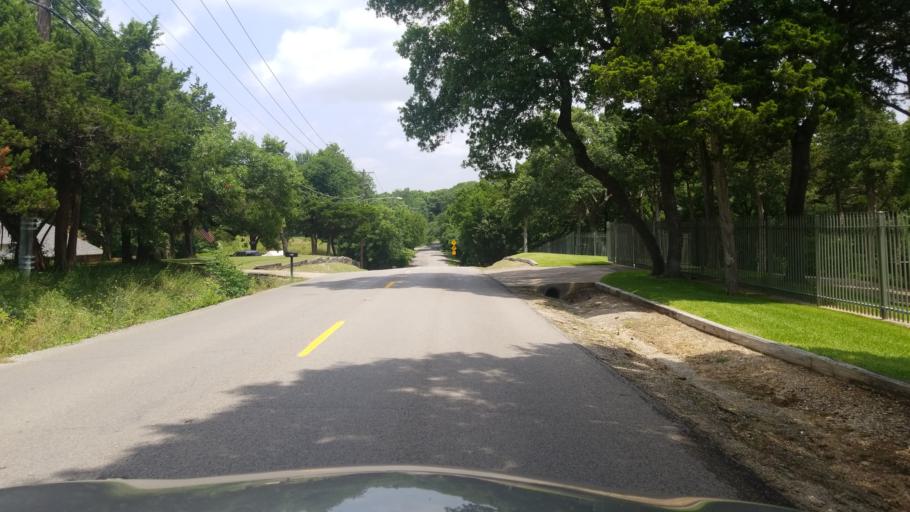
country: US
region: Texas
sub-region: Dallas County
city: Duncanville
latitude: 32.6772
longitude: -96.9258
